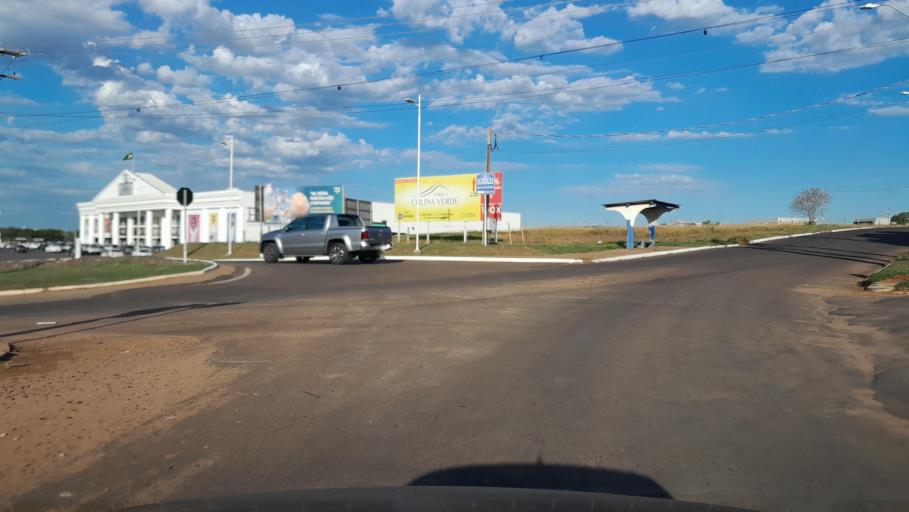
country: BR
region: Parana
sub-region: Umuarama
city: Umuarama
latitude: -23.7799
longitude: -53.3025
